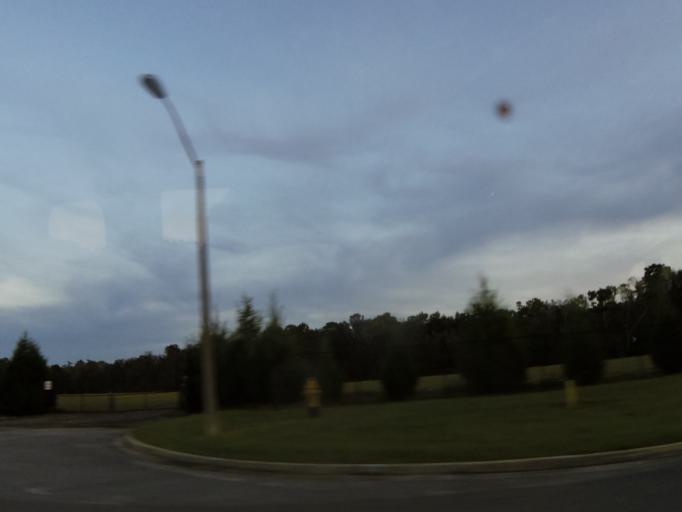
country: US
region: Florida
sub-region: Saint Johns County
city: Fruit Cove
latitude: 30.1544
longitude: -81.5202
